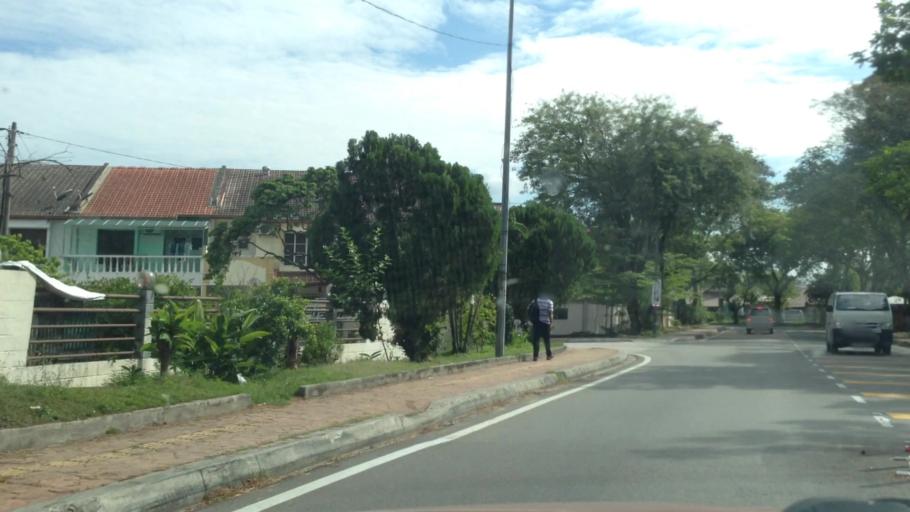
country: MY
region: Selangor
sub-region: Petaling
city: Petaling Jaya
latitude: 3.0774
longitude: 101.6210
